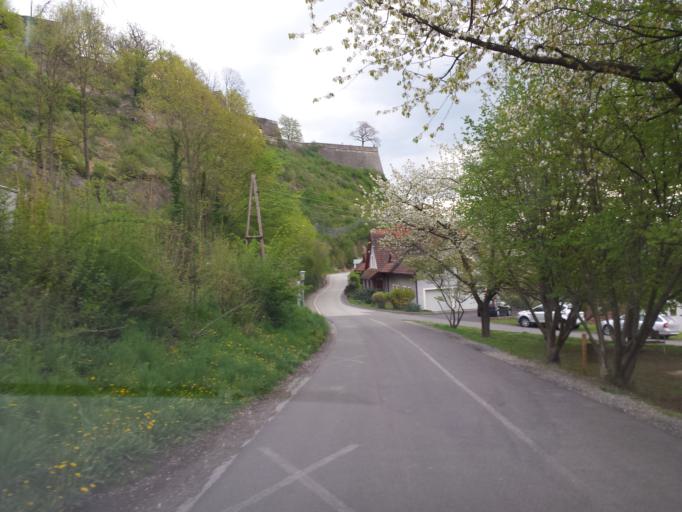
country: AT
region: Styria
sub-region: Politischer Bezirk Suedoststeiermark
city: Riegersburg
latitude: 47.0034
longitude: 15.9307
